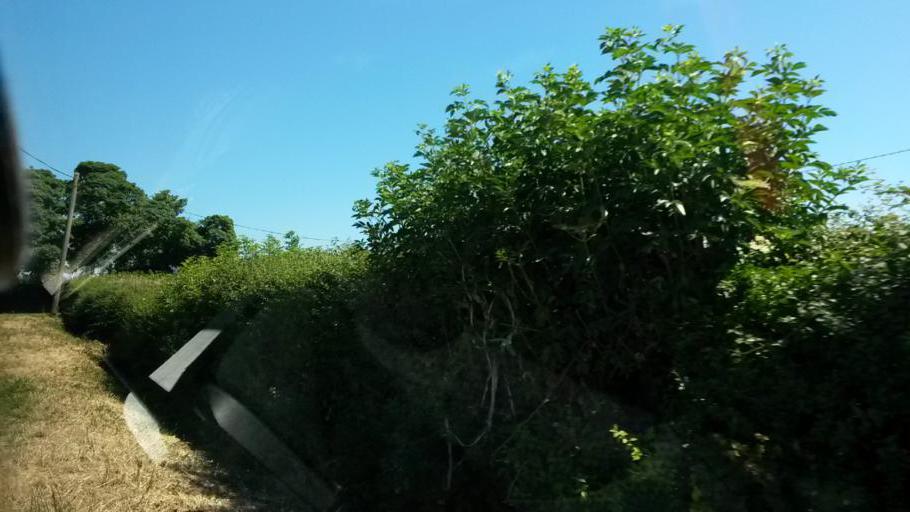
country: IE
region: Leinster
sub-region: Dublin City
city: Finglas
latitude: 53.4383
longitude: -6.3106
